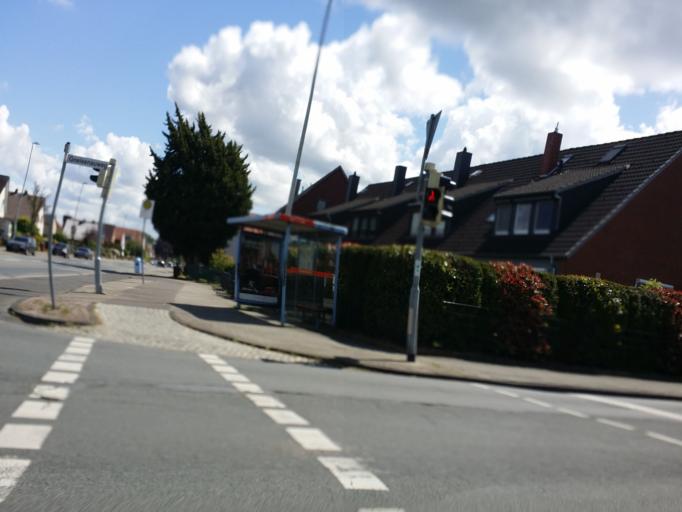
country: DE
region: Lower Saxony
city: Delmenhorst
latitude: 53.0278
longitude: 8.6315
